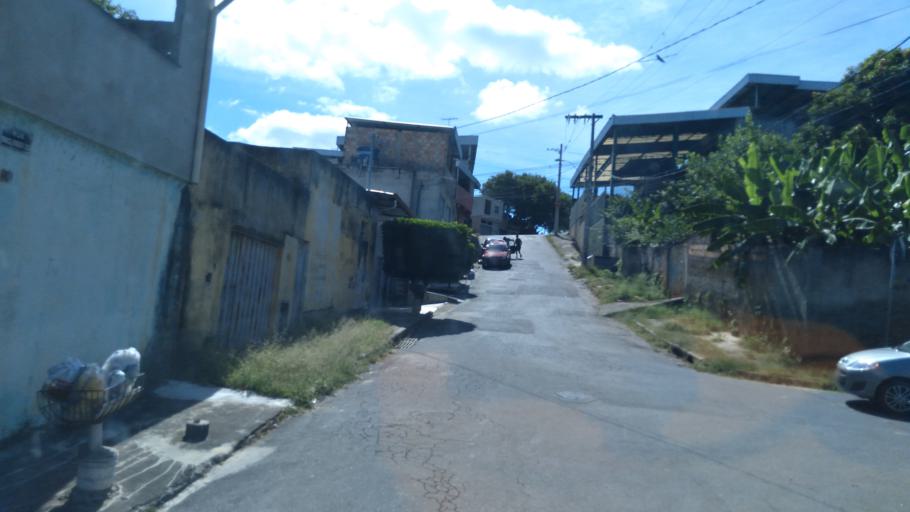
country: BR
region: Minas Gerais
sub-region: Belo Horizonte
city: Belo Horizonte
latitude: -19.8491
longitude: -43.9012
